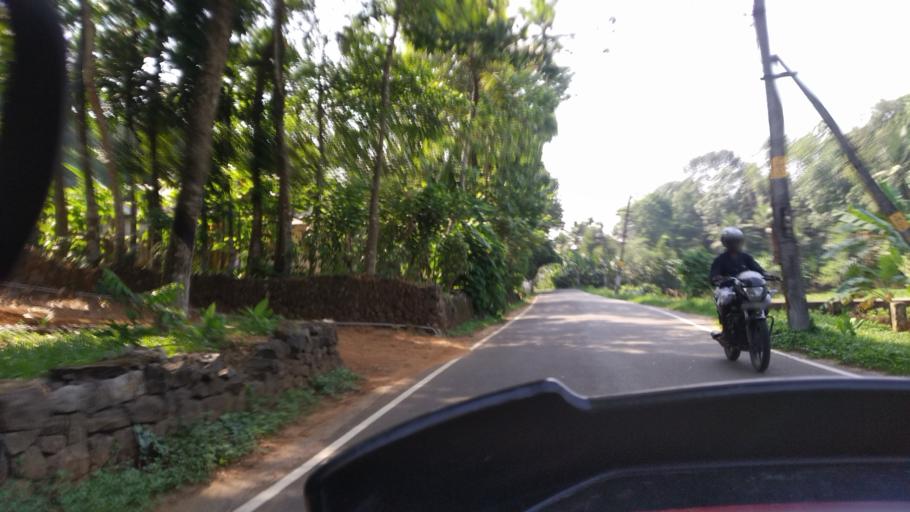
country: IN
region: Kerala
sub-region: Ernakulam
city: Piravam
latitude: 9.8127
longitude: 76.5663
